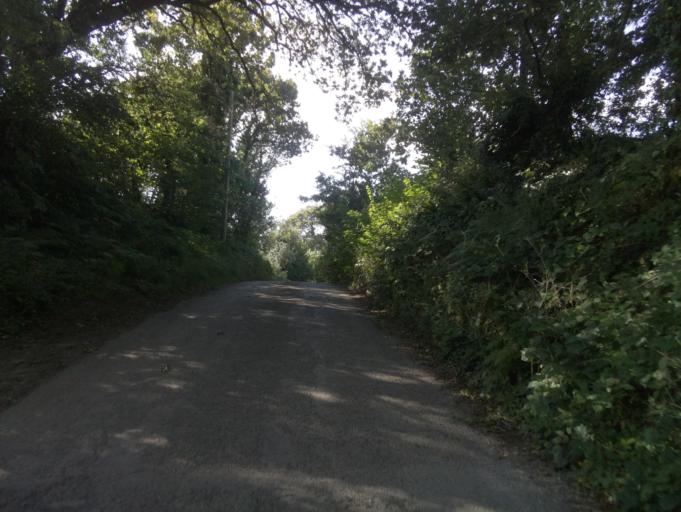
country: GB
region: England
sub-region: Devon
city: Buckfastleigh
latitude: 50.4387
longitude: -3.7826
